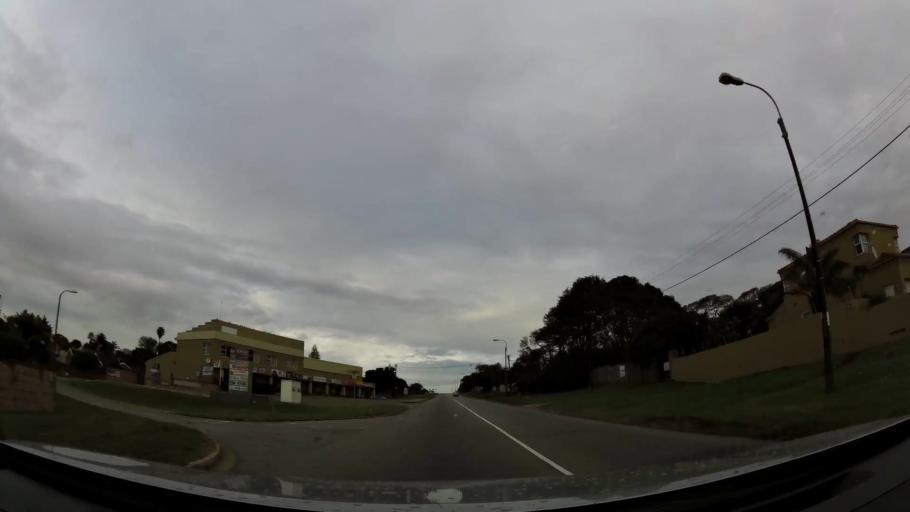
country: ZA
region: Eastern Cape
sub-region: Nelson Mandela Bay Metropolitan Municipality
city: Port Elizabeth
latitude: -33.9957
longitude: 25.5314
